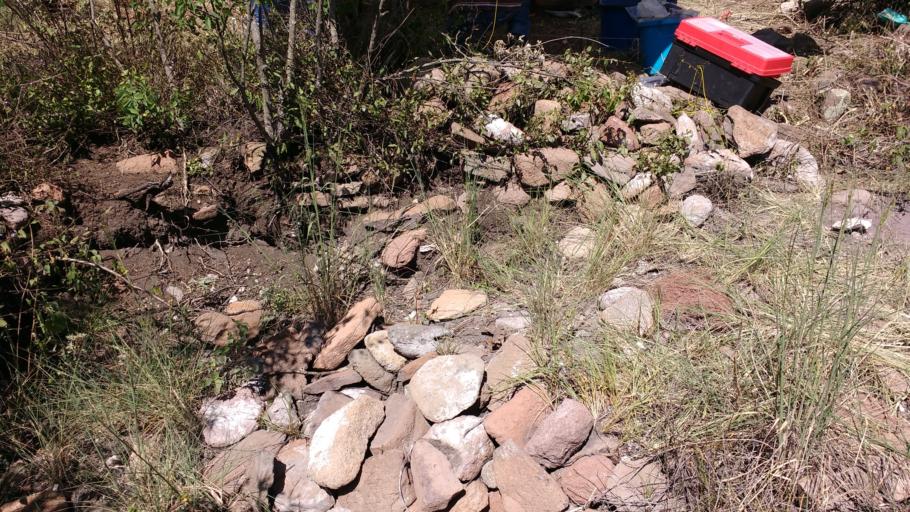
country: MX
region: Hidalgo
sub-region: Tezontepec de Aldama
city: Tenango
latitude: 20.2412
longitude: -99.2771
